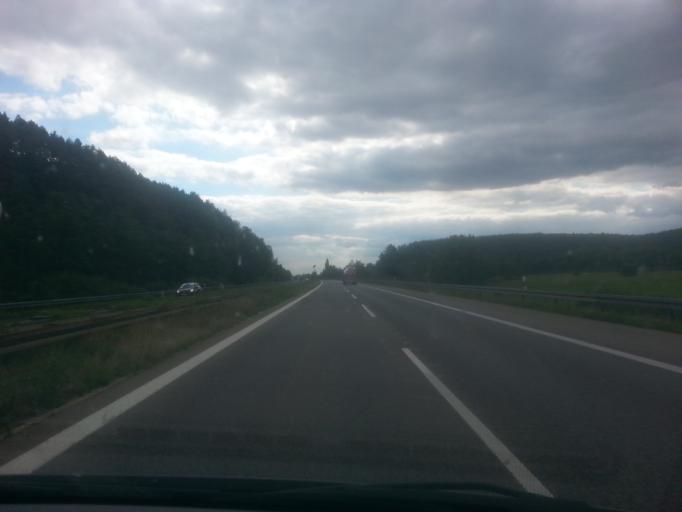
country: DE
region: Bavaria
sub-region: Upper Palatinate
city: Nabburg
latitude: 49.4275
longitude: 12.1731
